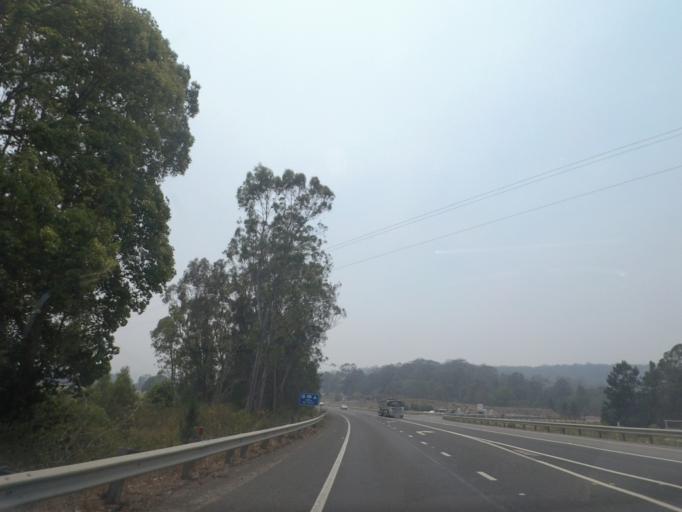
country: AU
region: New South Wales
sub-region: Clarence Valley
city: Maclean
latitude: -29.5639
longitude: 153.1462
